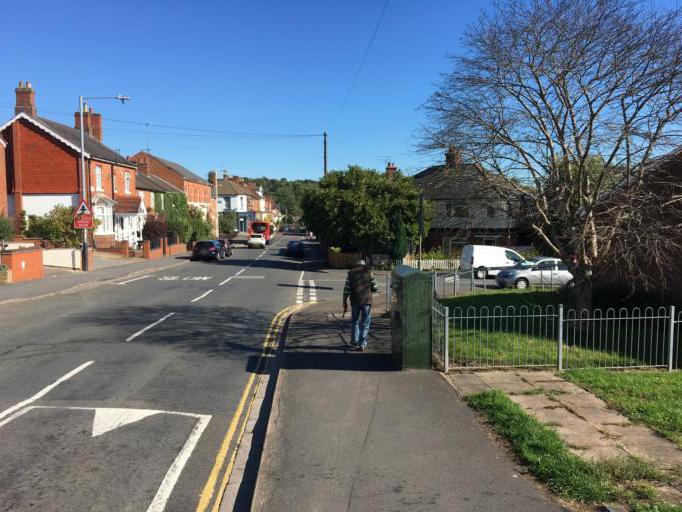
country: GB
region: England
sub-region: Warwickshire
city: Kenilworth
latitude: 52.3495
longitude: -1.5725
